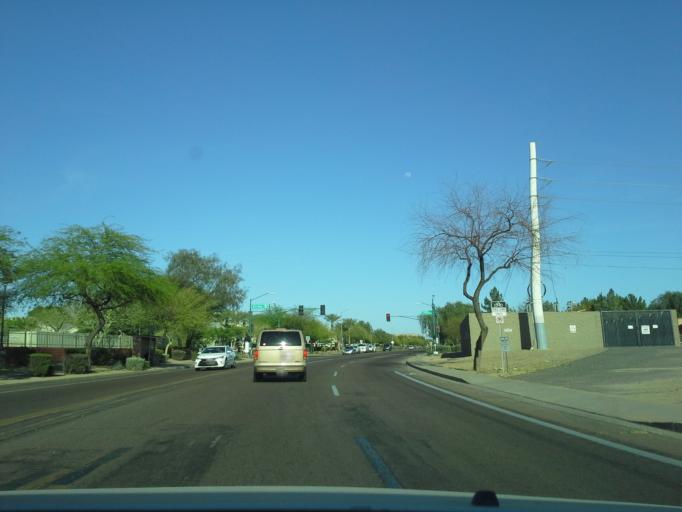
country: US
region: Arizona
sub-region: Maricopa County
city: Glendale
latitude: 33.6626
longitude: -112.1270
